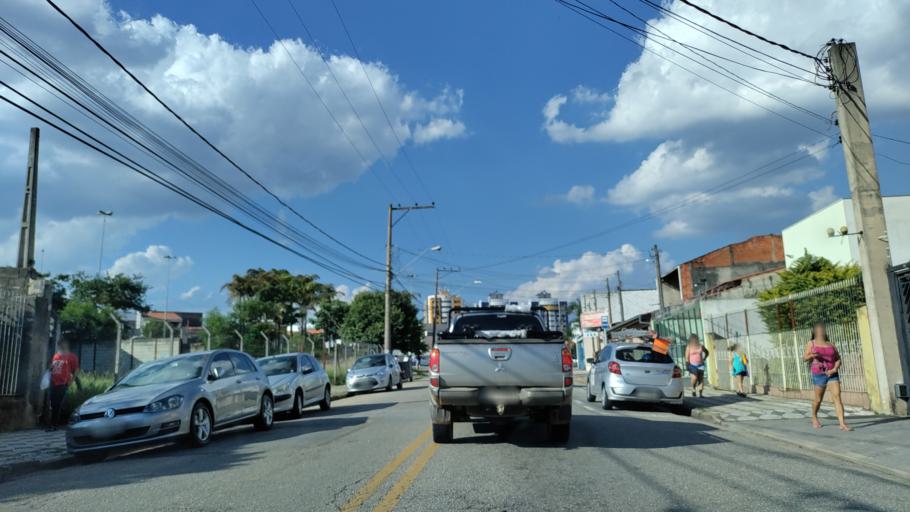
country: BR
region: Sao Paulo
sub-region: Sorocaba
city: Sorocaba
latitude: -23.4889
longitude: -47.4786
